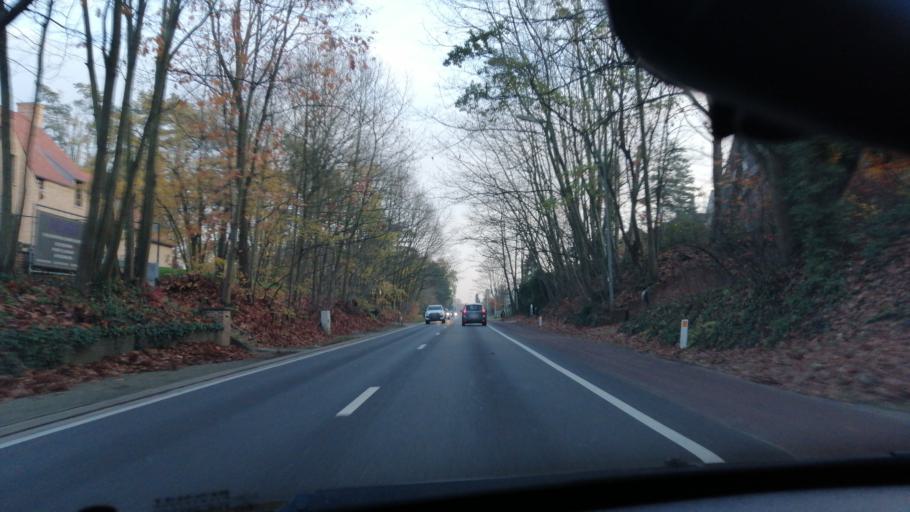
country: BE
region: Flanders
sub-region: Provincie Antwerpen
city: Herentals
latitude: 51.1942
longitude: 4.8279
